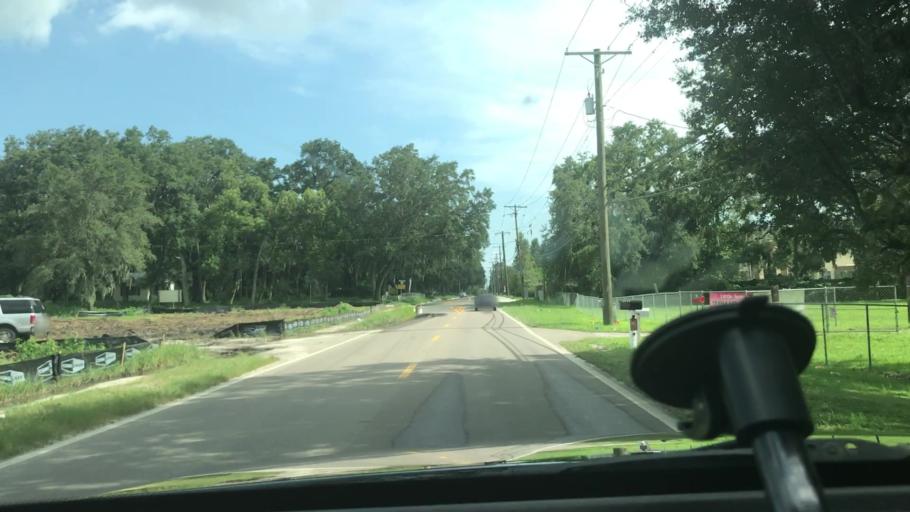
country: US
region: Florida
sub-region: Hillsborough County
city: Mango
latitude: 27.9932
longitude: -82.3188
